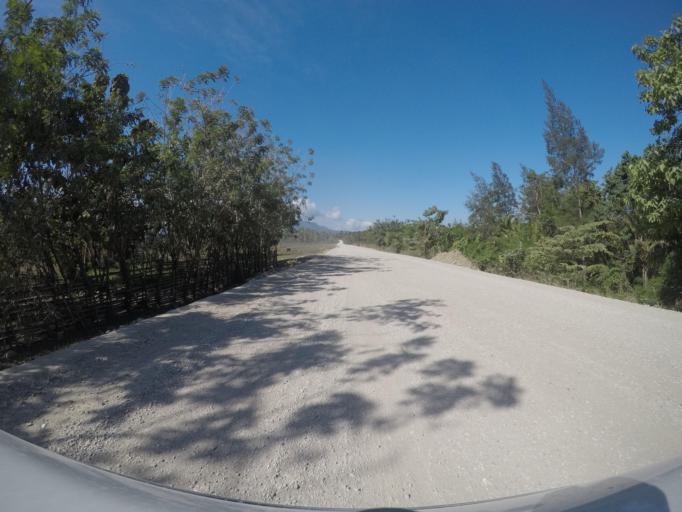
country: TL
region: Viqueque
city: Viqueque
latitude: -8.8310
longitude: 126.5223
